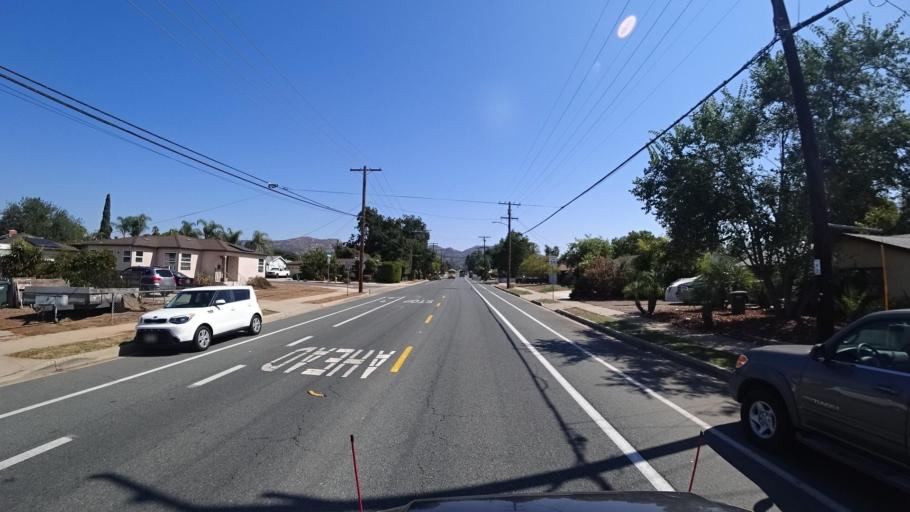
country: US
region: California
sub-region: San Diego County
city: Bostonia
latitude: 32.8002
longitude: -116.9263
